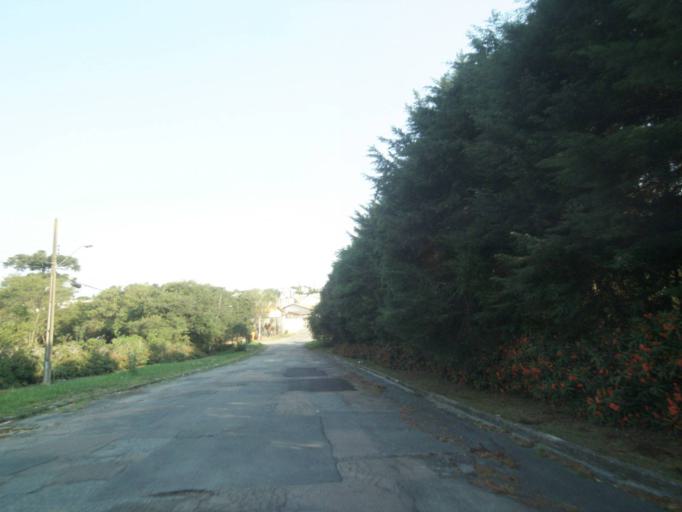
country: BR
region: Parana
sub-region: Curitiba
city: Curitiba
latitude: -25.4911
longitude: -49.2664
